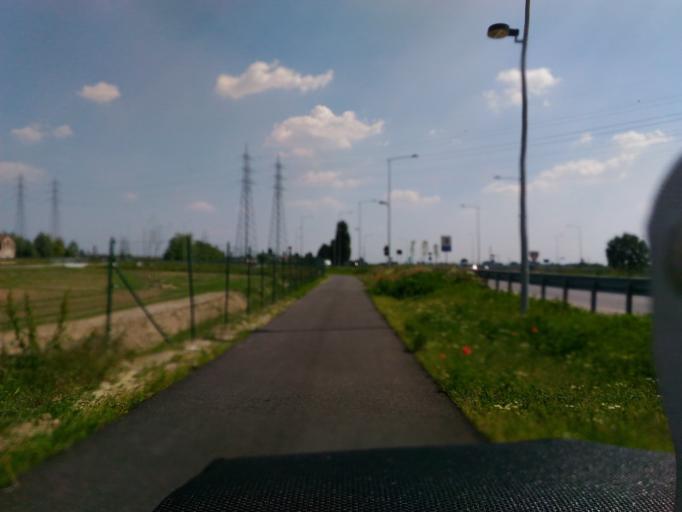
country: IT
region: Lombardy
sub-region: Citta metropolitana di Milano
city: Dresano
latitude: 45.3636
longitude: 9.3647
